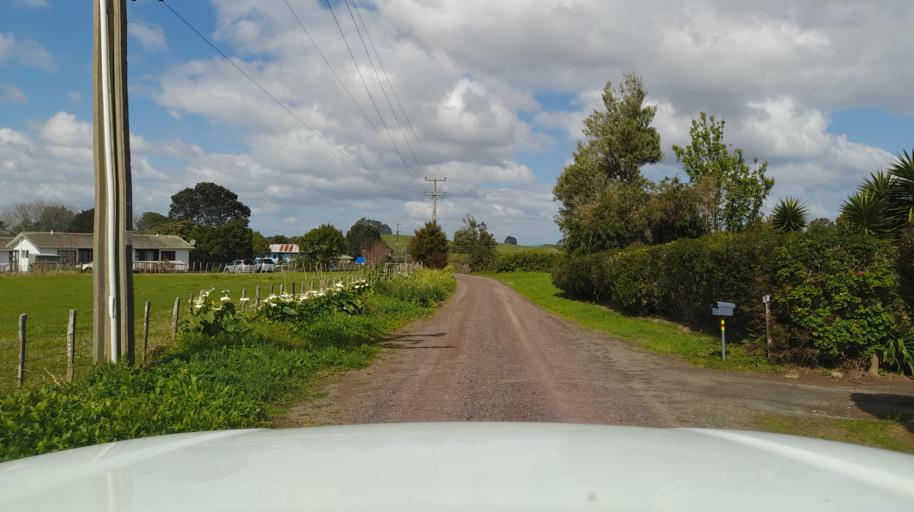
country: NZ
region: Northland
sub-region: Far North District
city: Waimate North
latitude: -35.3740
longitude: 173.8600
